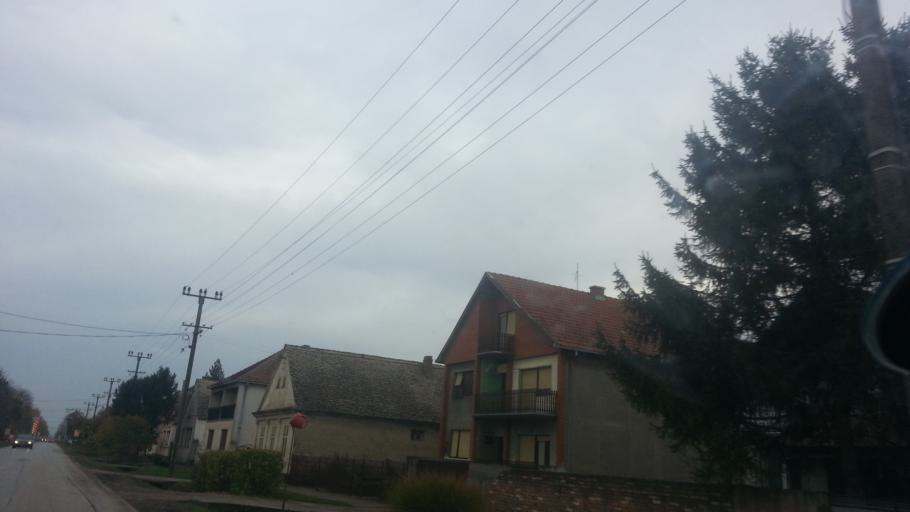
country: RS
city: Golubinci
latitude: 44.9852
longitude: 20.0594
